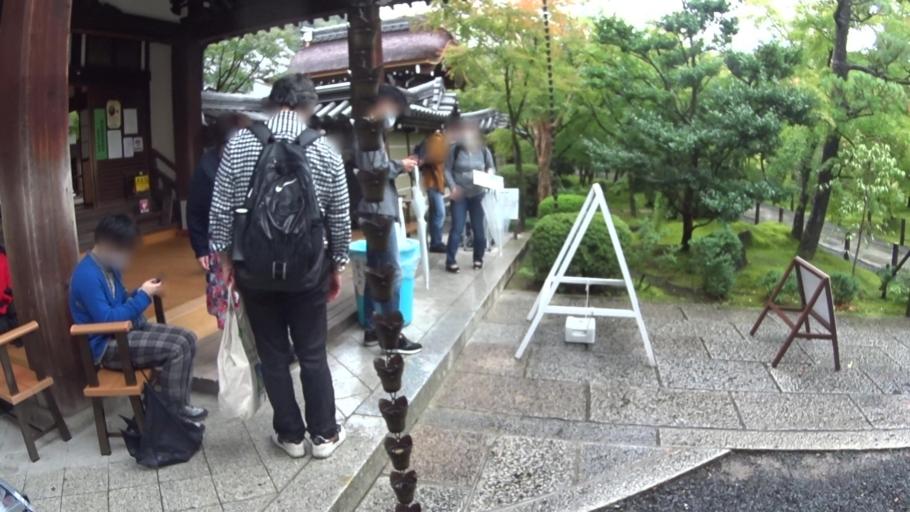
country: JP
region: Kyoto
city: Kyoto
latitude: 34.9893
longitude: 135.8074
